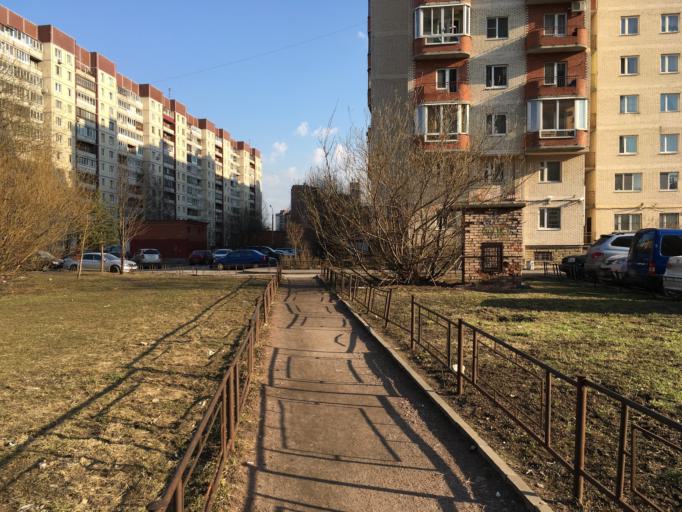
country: RU
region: St.-Petersburg
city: Komendantsky aerodrom
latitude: 60.0149
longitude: 30.2533
